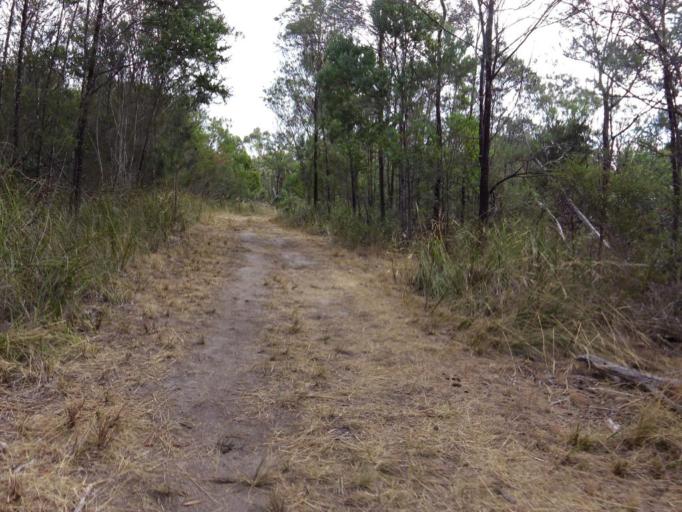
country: AU
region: Victoria
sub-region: Frankston
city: Frankston South
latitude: -38.1795
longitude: 145.1279
